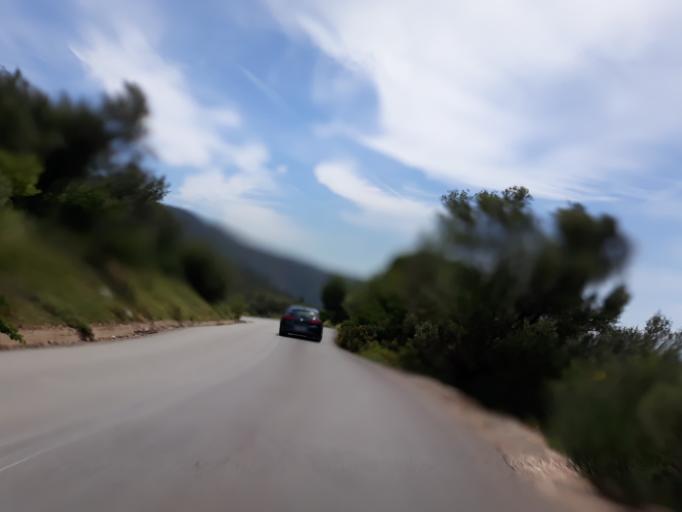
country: GR
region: Attica
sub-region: Nomarchia Dytikis Attikis
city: Magoula
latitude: 38.1497
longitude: 23.5215
